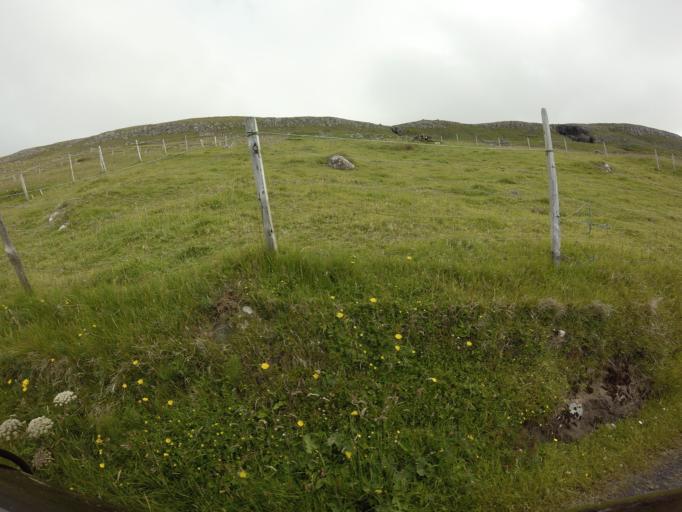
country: FO
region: Sandoy
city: Sandur
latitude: 61.7959
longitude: -6.7499
